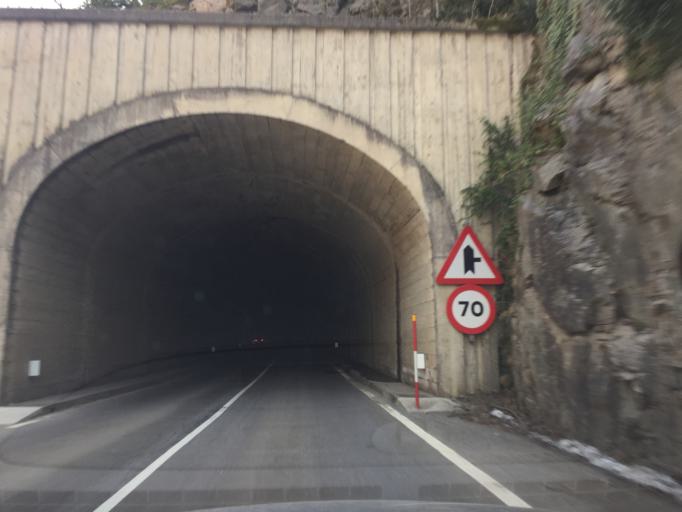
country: ES
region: Aragon
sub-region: Provincia de Huesca
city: Bielsa
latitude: 42.6415
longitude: 0.2145
